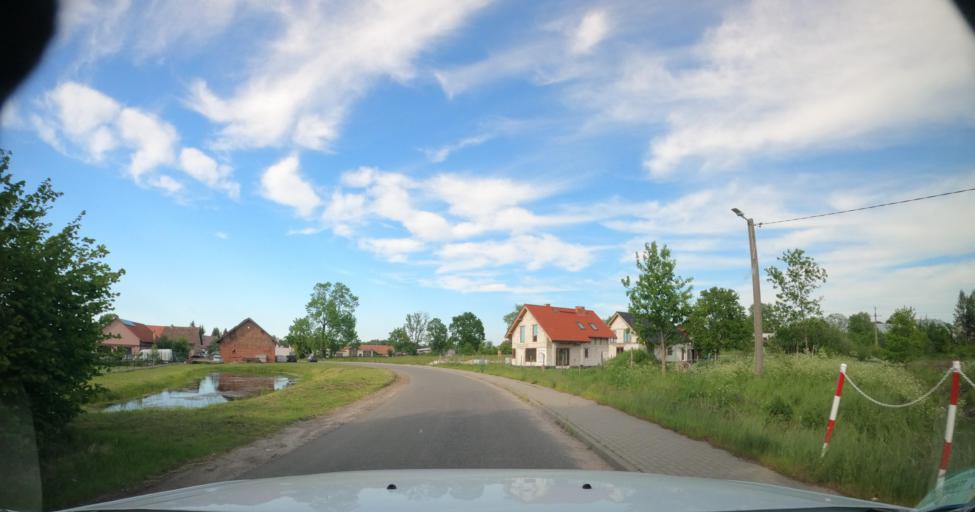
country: PL
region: Warmian-Masurian Voivodeship
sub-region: Powiat ostrodzki
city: Morag
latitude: 54.0780
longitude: 19.9030
